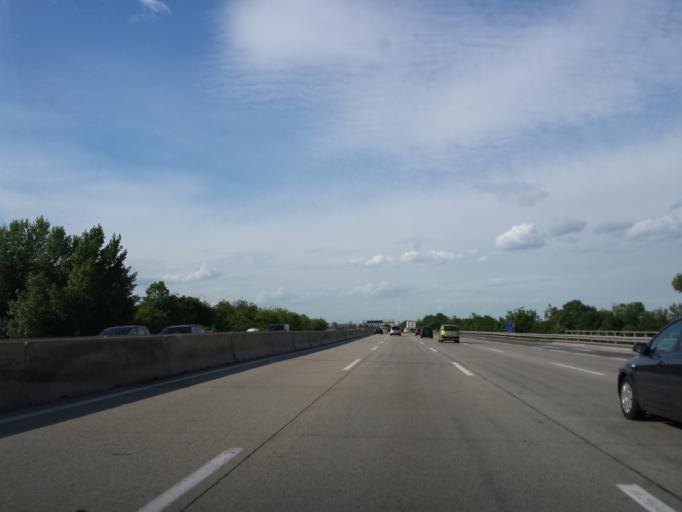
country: AT
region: Lower Austria
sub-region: Politischer Bezirk Modling
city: Guntramsdorf
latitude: 48.0421
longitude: 16.3418
